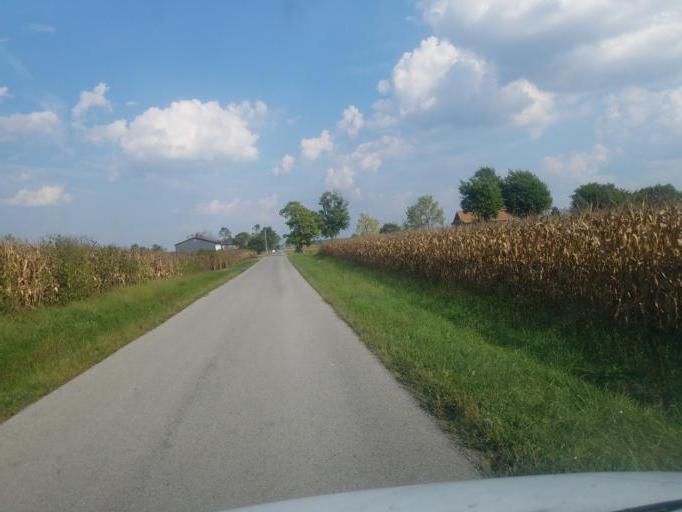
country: US
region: Ohio
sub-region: Hancock County
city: Arlington
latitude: 40.8194
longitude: -83.6365
